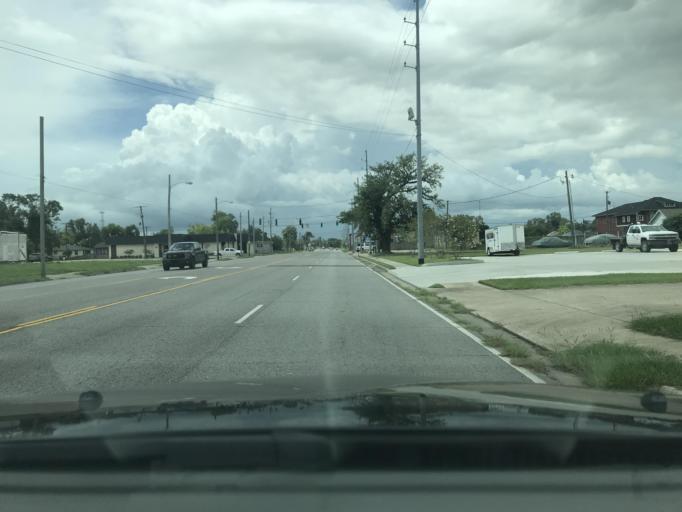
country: US
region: Louisiana
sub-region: Calcasieu Parish
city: Lake Charles
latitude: 30.2328
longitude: -93.2044
